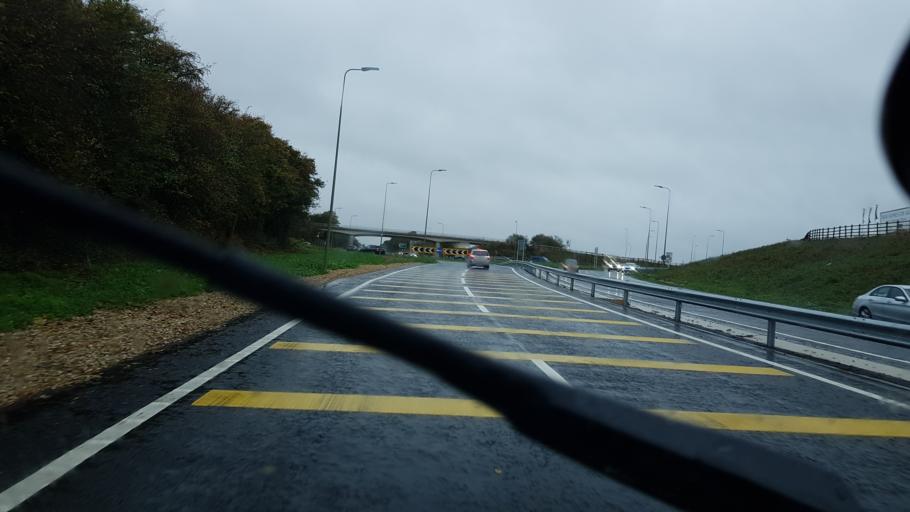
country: GB
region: England
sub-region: Oxfordshire
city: Witney
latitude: 51.7788
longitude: -1.5223
